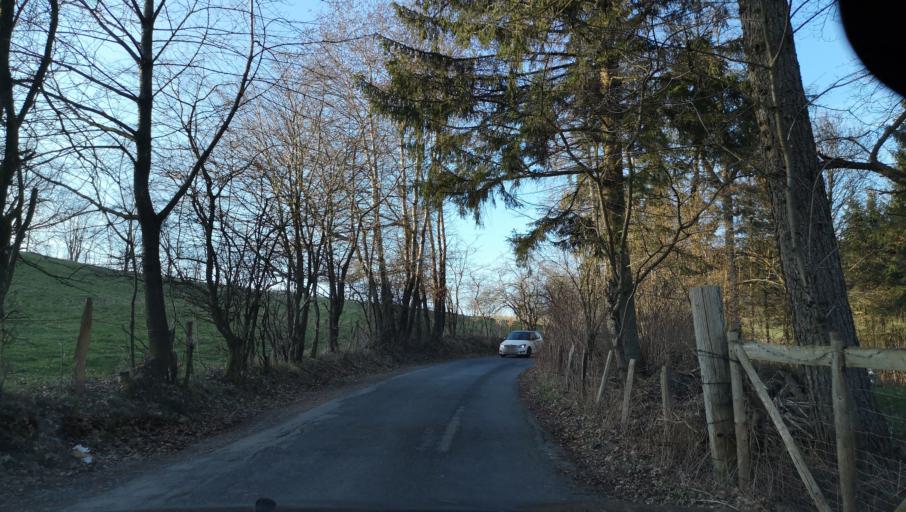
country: DE
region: North Rhine-Westphalia
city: Radevormwald
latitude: 51.1965
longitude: 7.2911
